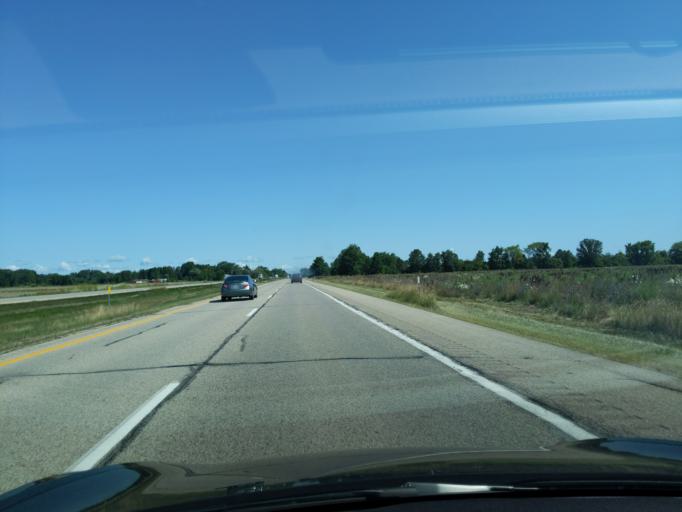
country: US
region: Michigan
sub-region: Gratiot County
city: Ithaca
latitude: 43.1948
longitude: -84.5633
